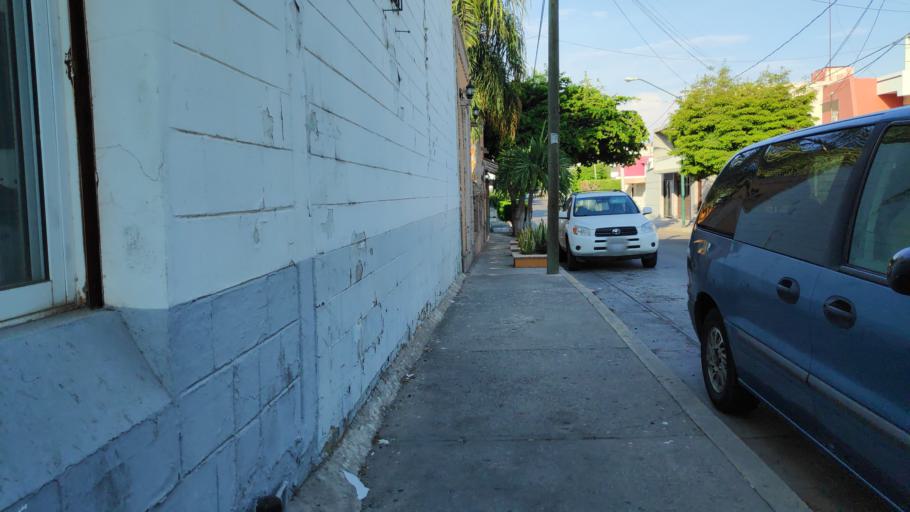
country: MX
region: Sinaloa
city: Culiacan
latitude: 24.7898
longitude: -107.4004
